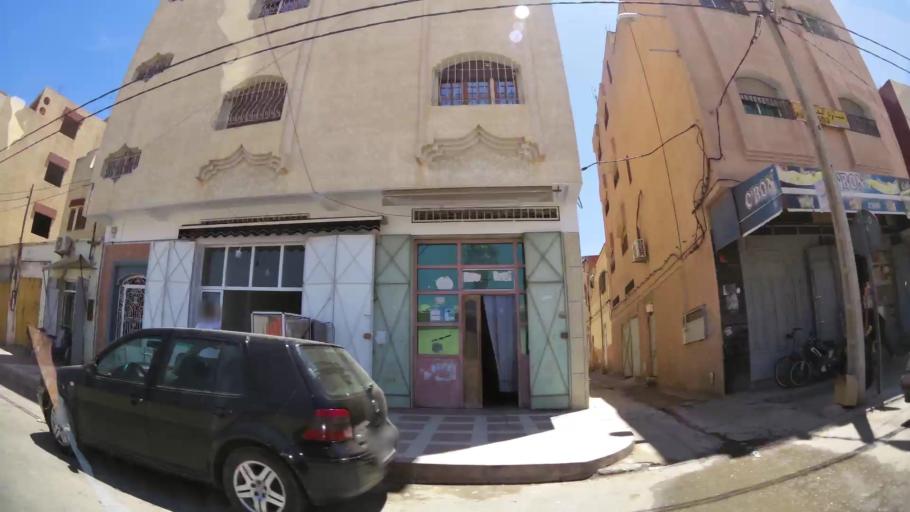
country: MA
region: Oriental
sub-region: Oujda-Angad
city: Oujda
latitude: 34.6742
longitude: -1.9286
